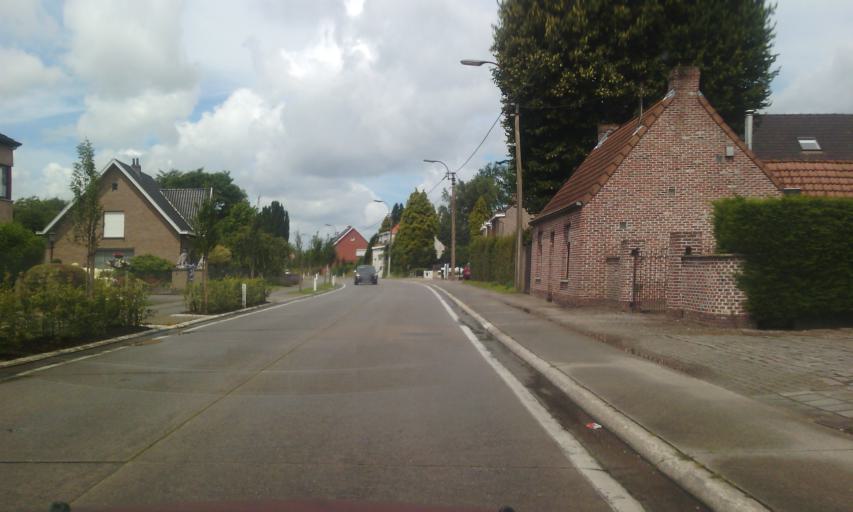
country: BE
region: Flanders
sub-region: Provincie Oost-Vlaanderen
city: Laarne
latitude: 51.0237
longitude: 3.8654
